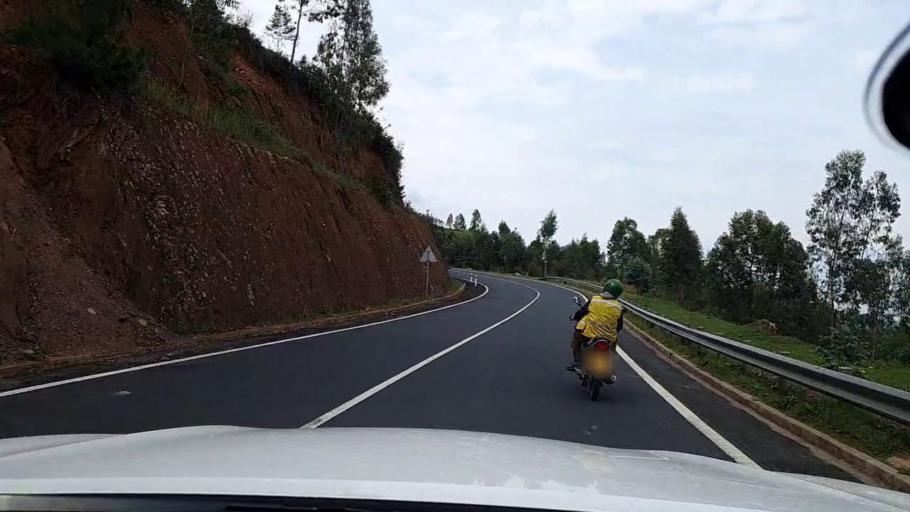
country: RW
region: Western Province
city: Kibuye
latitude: -2.1743
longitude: 29.2924
